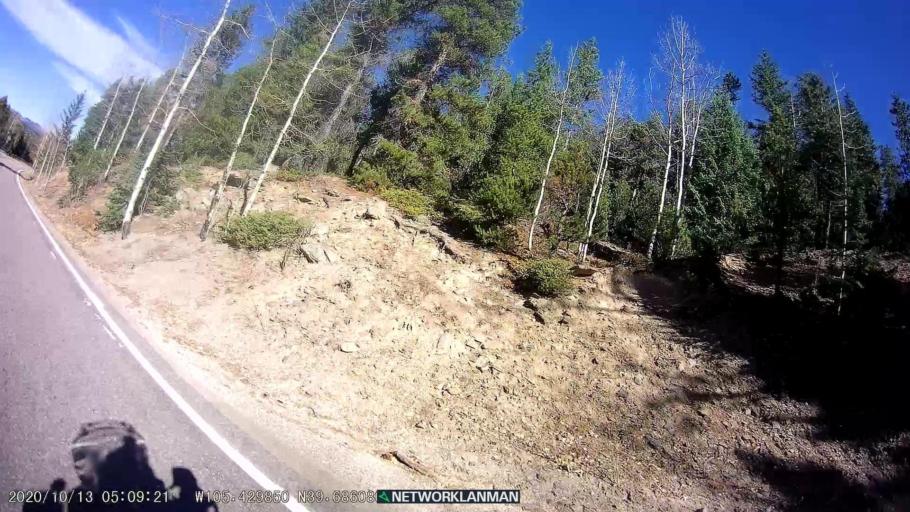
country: US
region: Colorado
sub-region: Clear Creek County
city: Idaho Springs
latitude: 39.6863
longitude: -105.4297
